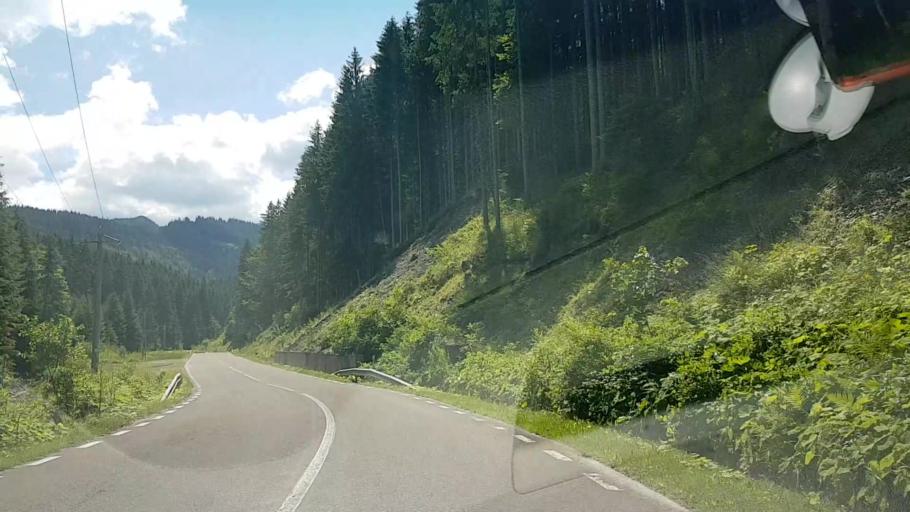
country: RO
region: Suceava
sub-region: Comuna Sadova
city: Sadova
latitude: 47.4761
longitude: 25.4992
